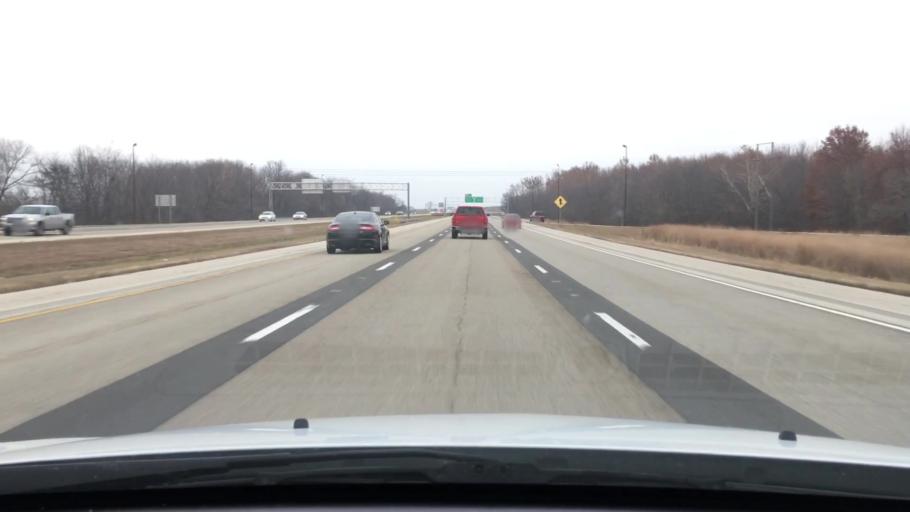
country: US
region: Illinois
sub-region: Logan County
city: Lincoln
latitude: 40.1633
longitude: -89.4176
